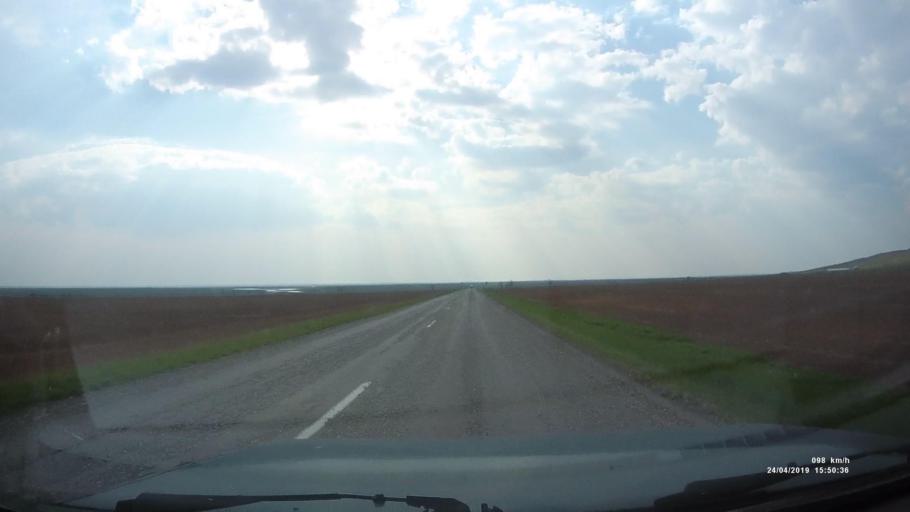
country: RU
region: Kalmykiya
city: Yashalta
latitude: 46.6042
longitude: 42.6294
